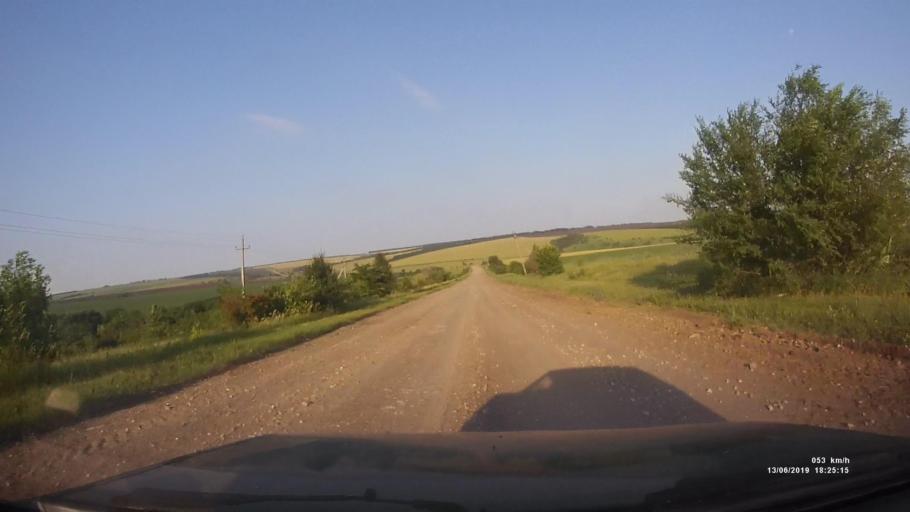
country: RU
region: Rostov
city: Kazanskaya
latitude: 49.8510
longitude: 41.2987
